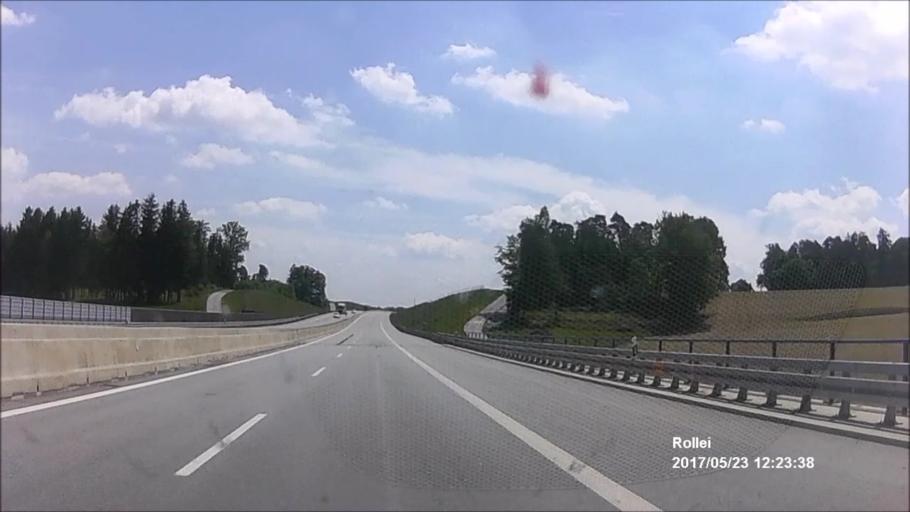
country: DE
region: Bavaria
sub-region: Lower Bavaria
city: Ergoldsbach
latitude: 48.6864
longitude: 12.1847
